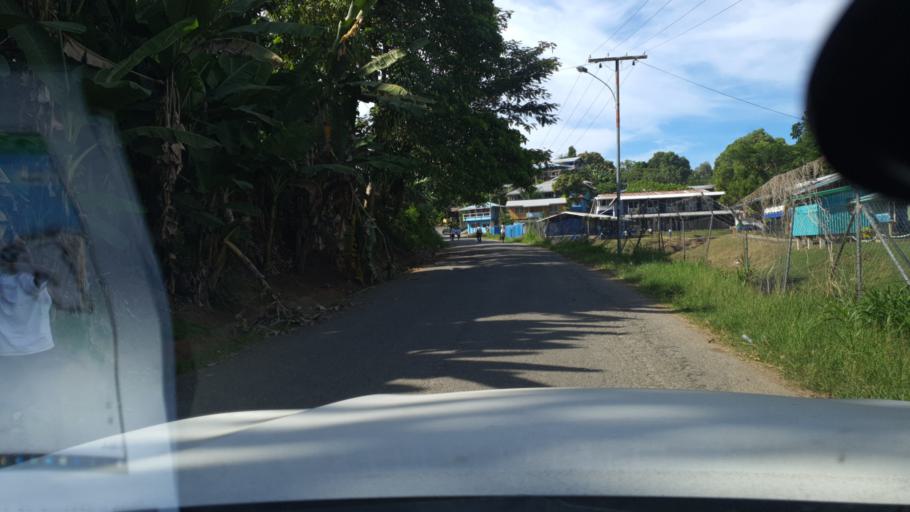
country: SB
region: Guadalcanal
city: Honiara
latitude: -9.4376
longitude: 159.9569
